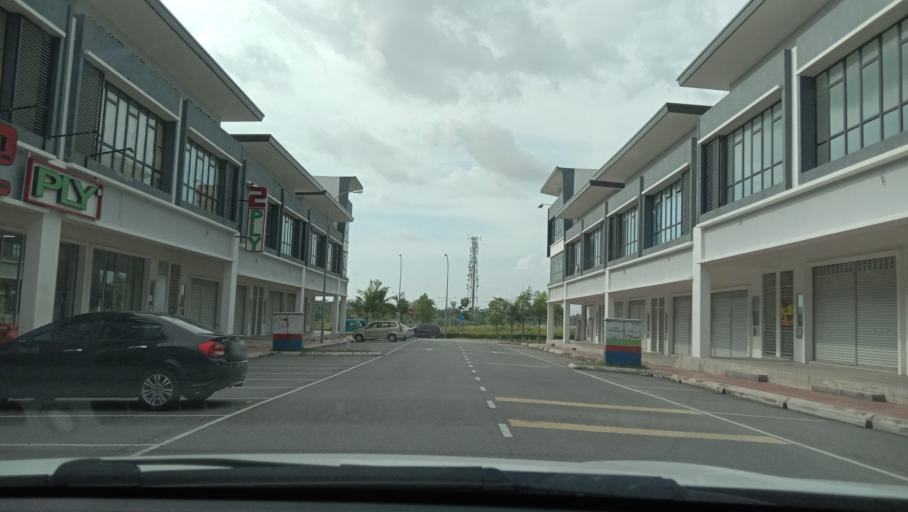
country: MY
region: Selangor
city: Ladang Seri Kundang
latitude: 3.2428
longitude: 101.4754
